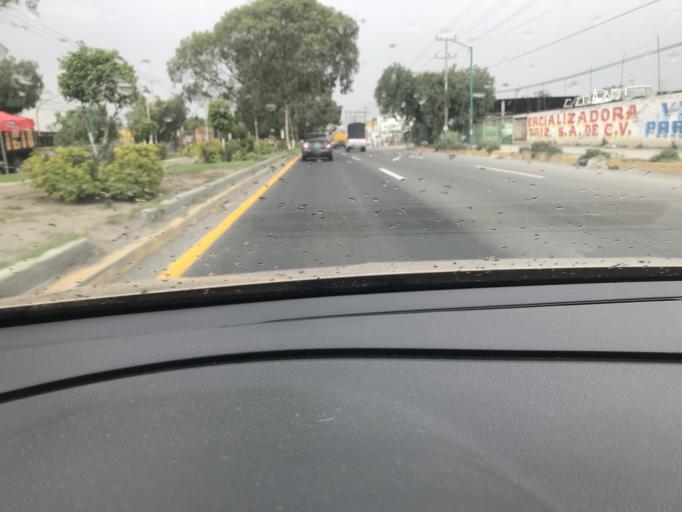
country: MX
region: Mexico
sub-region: La Paz
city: Arenal
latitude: 19.3871
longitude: -98.9372
